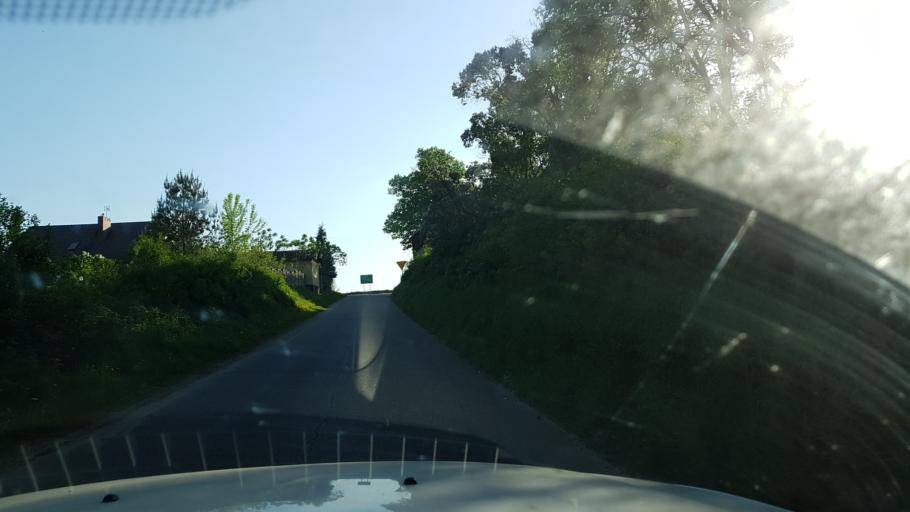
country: PL
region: West Pomeranian Voivodeship
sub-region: Powiat lobeski
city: Dobra
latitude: 53.6346
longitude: 15.3605
